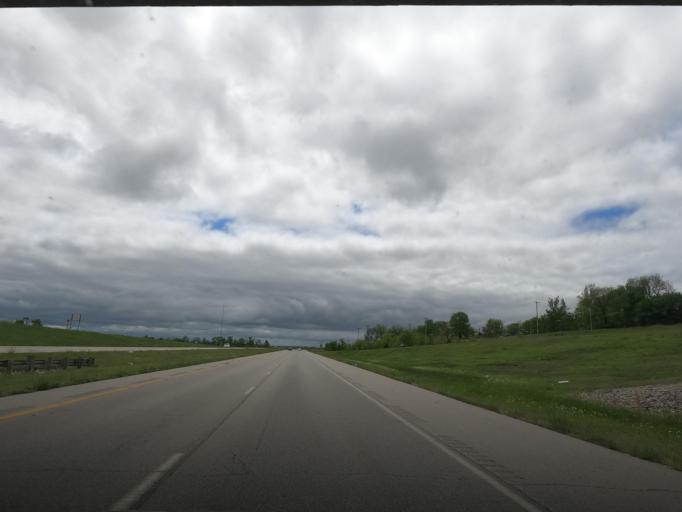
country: US
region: Kansas
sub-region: Wilson County
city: Neodesha
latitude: 37.4132
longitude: -95.7106
